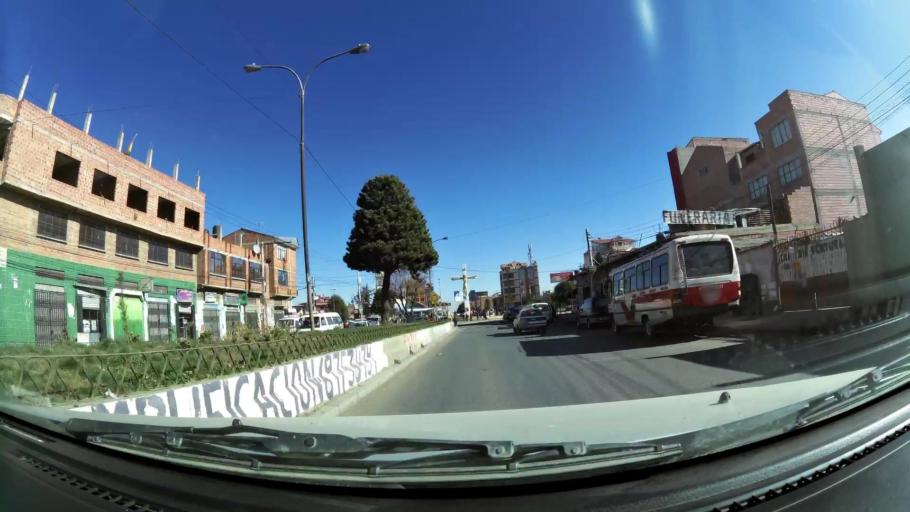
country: BO
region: La Paz
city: La Paz
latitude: -16.5258
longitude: -68.1998
